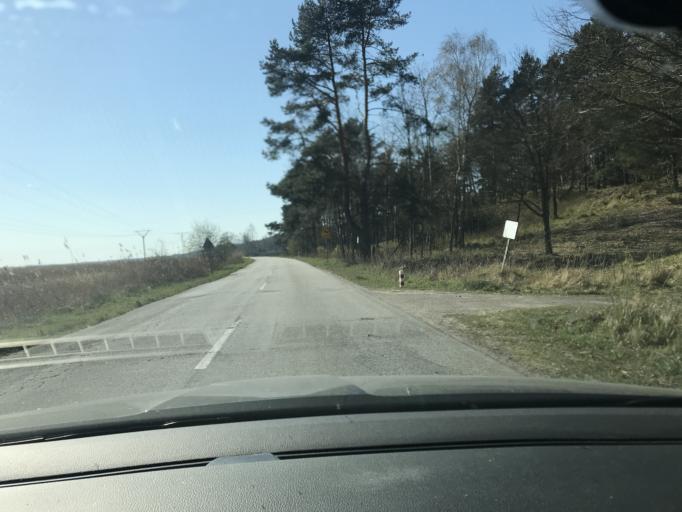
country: PL
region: Pomeranian Voivodeship
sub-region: Powiat nowodworski
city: Sztutowo
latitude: 54.3527
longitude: 19.3007
